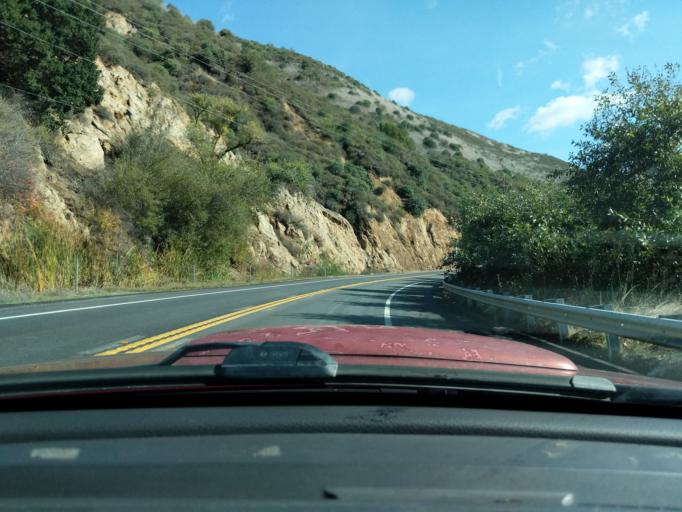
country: US
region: California
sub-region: San Benito County
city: Aromas
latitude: 36.9126
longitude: -121.6288
